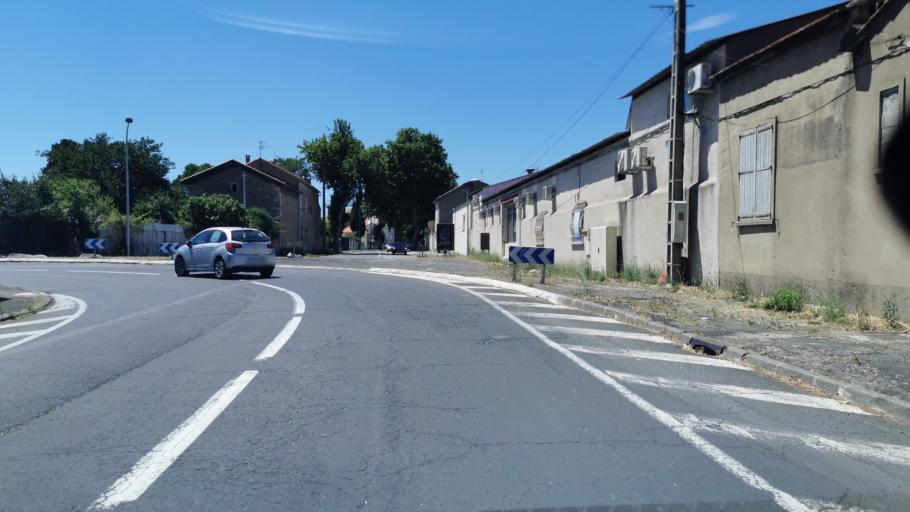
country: FR
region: Languedoc-Roussillon
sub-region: Departement de l'Herault
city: Beziers
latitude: 43.3378
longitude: 3.2023
